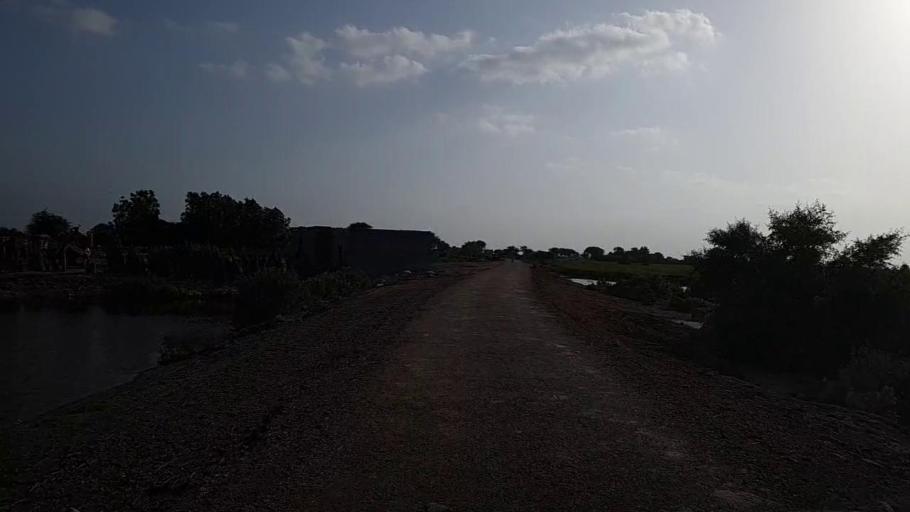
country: PK
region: Sindh
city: Kario
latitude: 24.6706
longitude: 68.4567
